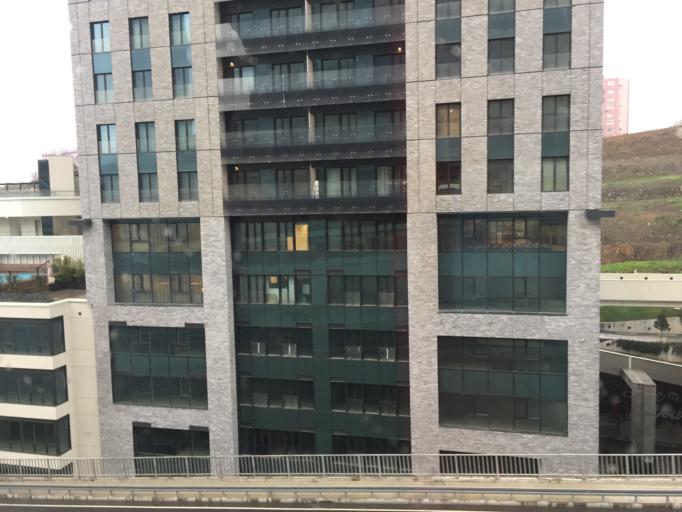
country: TR
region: Istanbul
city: Sisli
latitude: 41.1047
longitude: 28.9921
